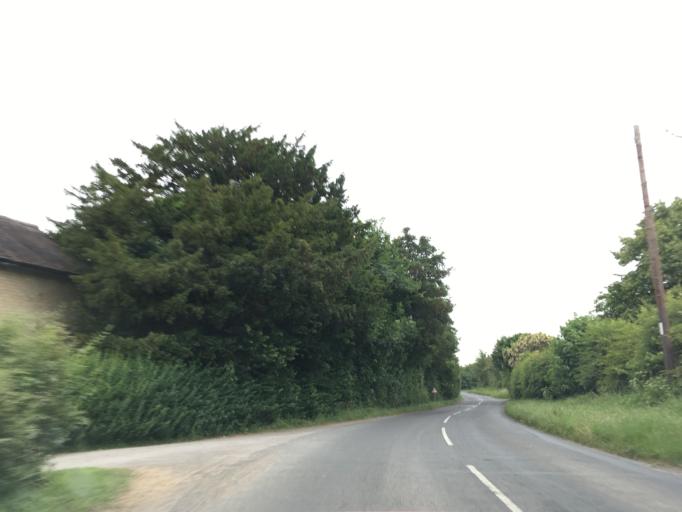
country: GB
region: England
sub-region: Gloucestershire
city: Stonehouse
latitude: 51.7792
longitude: -2.3472
